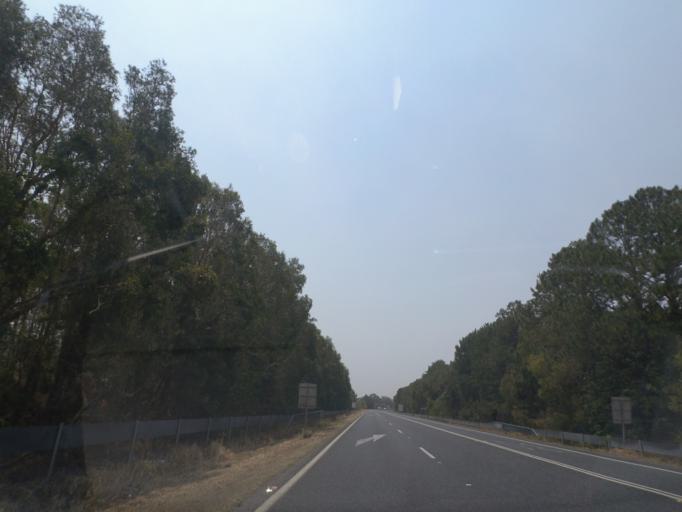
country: AU
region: New South Wales
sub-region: Ballina
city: Ballina
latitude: -28.9391
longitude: 153.4700
